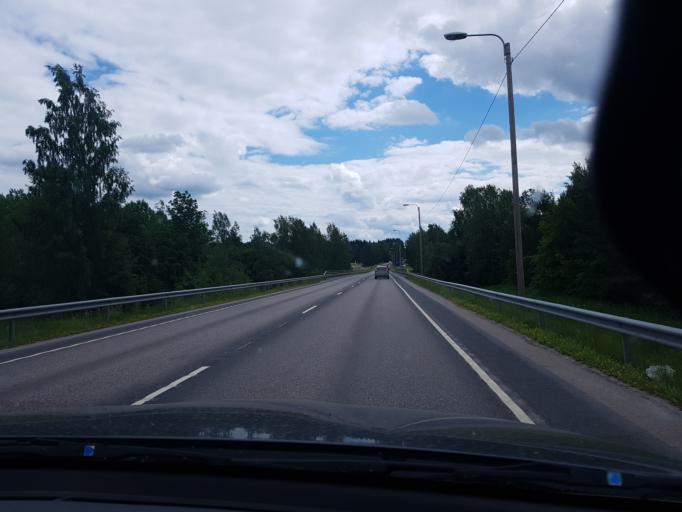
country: FI
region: Pirkanmaa
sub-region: Tampere
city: Paelkaene
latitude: 61.3375
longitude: 24.2788
